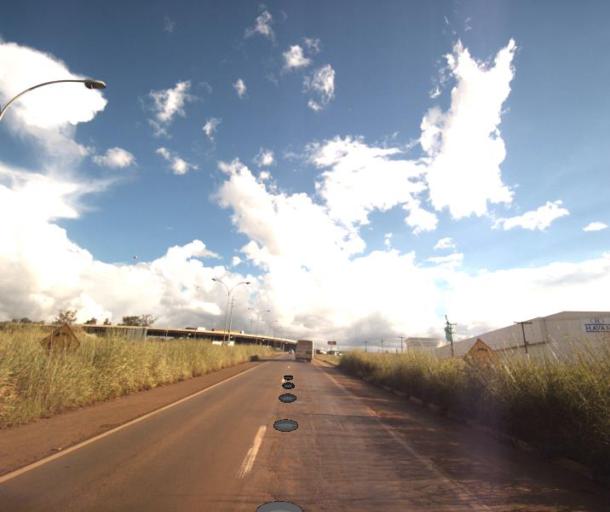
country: BR
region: Goias
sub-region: Anapolis
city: Anapolis
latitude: -16.3516
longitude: -48.9284
